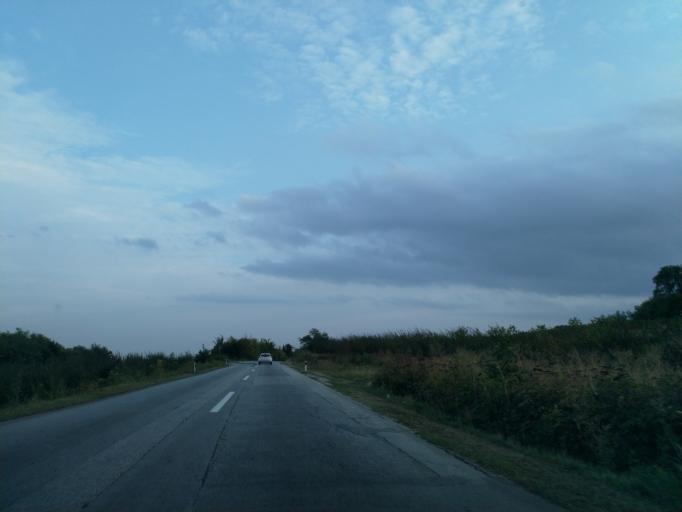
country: RS
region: Central Serbia
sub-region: Sumadijski Okrug
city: Topola
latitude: 44.1567
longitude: 20.7391
